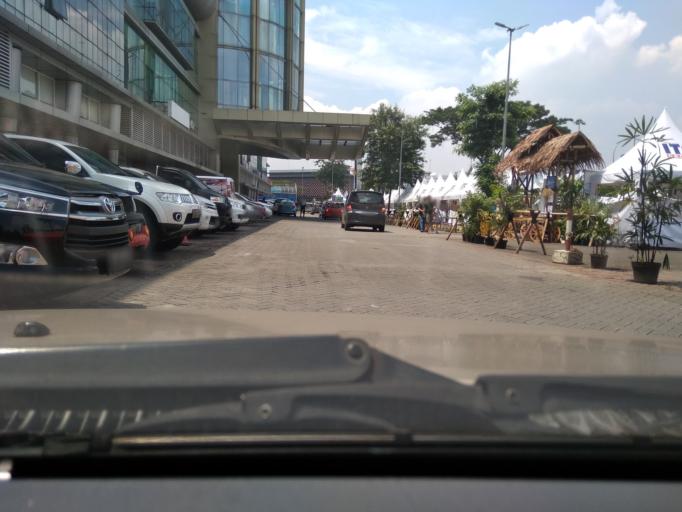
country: ID
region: West Java
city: Serpong
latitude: -6.2873
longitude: 106.6641
